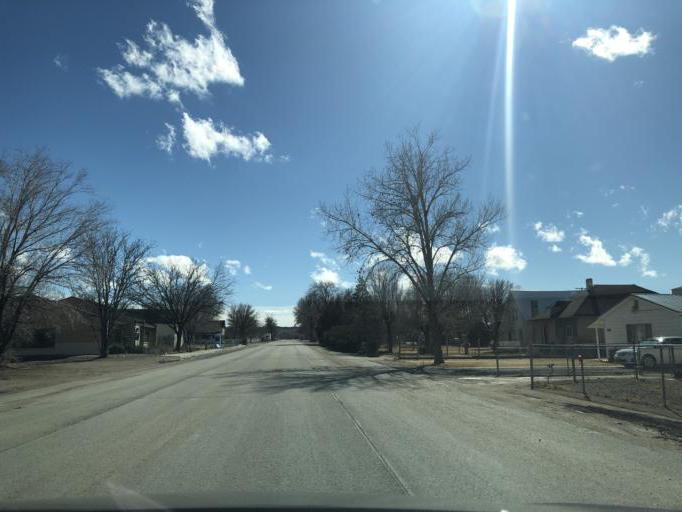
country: US
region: Utah
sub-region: Carbon County
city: East Carbon City
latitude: 38.9950
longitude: -110.1622
